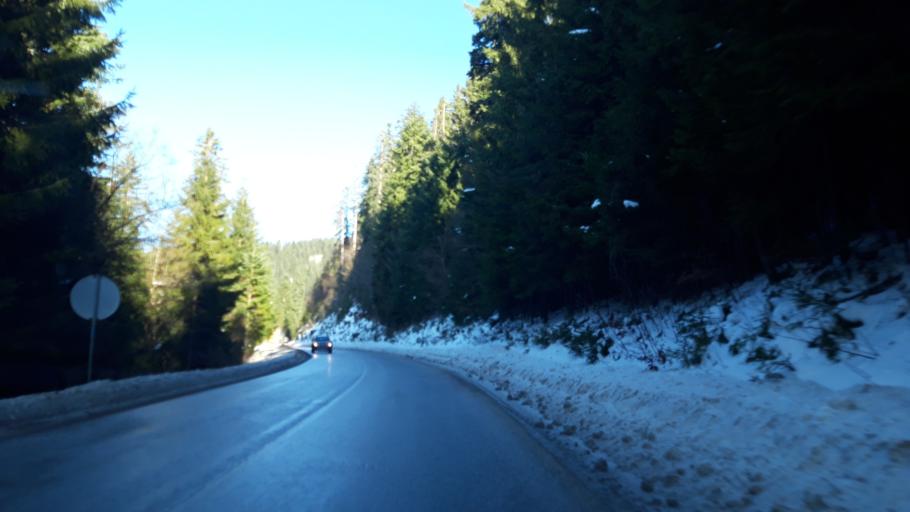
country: BA
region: Republika Srpska
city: Pale
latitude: 43.9155
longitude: 18.6481
